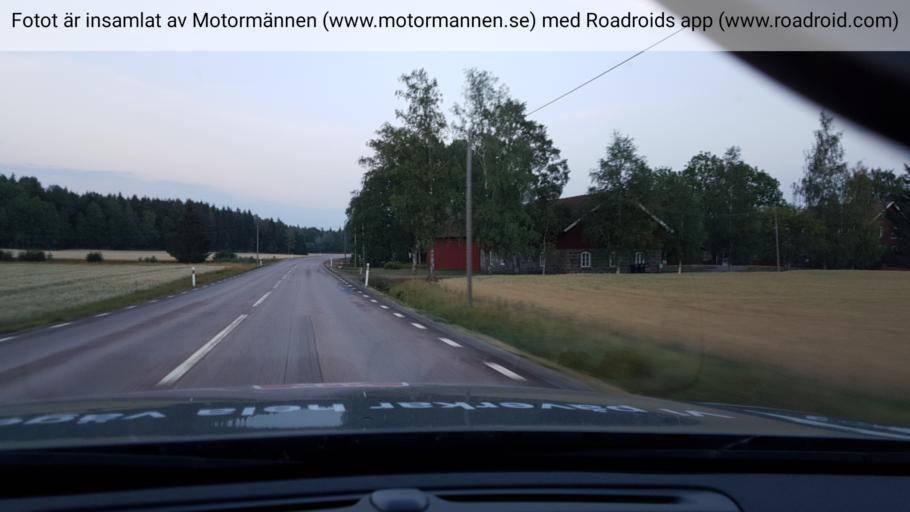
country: SE
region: Uppsala
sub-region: Heby Kommun
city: Heby
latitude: 59.8199
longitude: 16.7714
